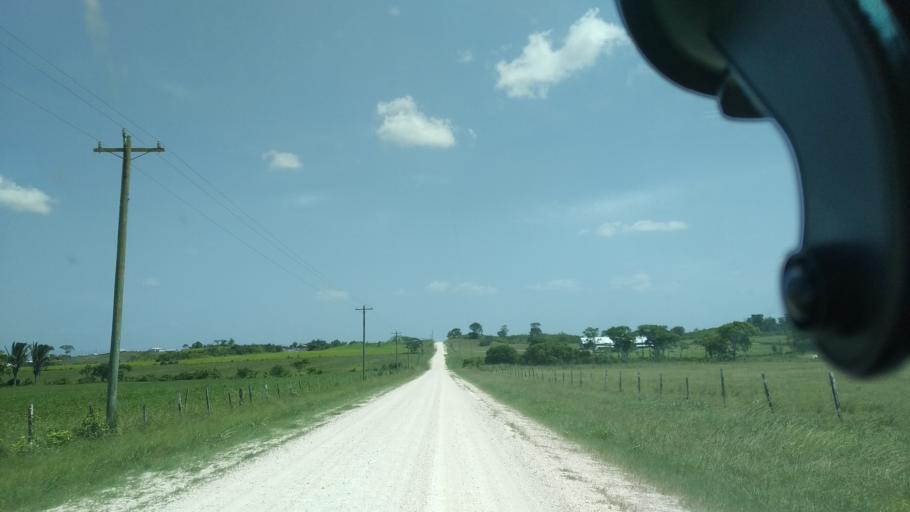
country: BZ
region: Cayo
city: San Ignacio
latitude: 17.3117
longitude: -89.0479
